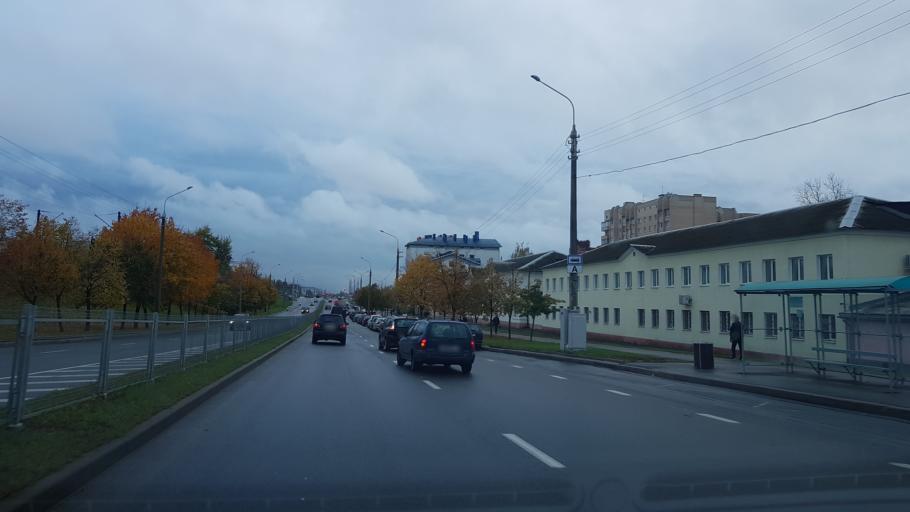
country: BY
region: Minsk
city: Minsk
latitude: 53.8770
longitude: 27.5621
